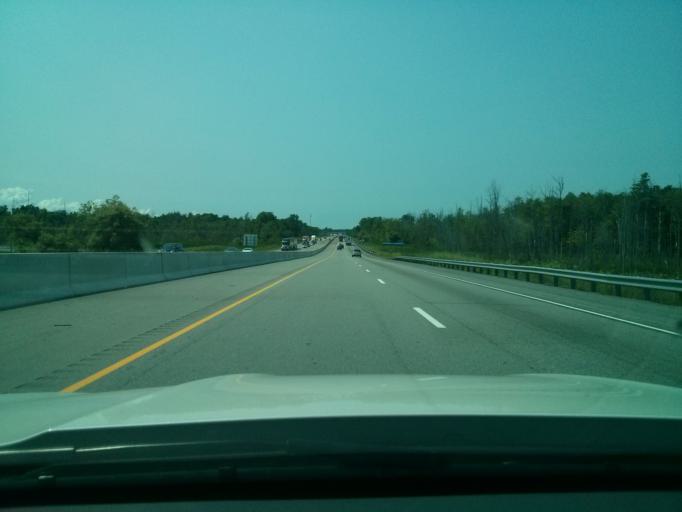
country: CA
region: Ontario
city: Prescott
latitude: 44.7347
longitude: -75.5079
